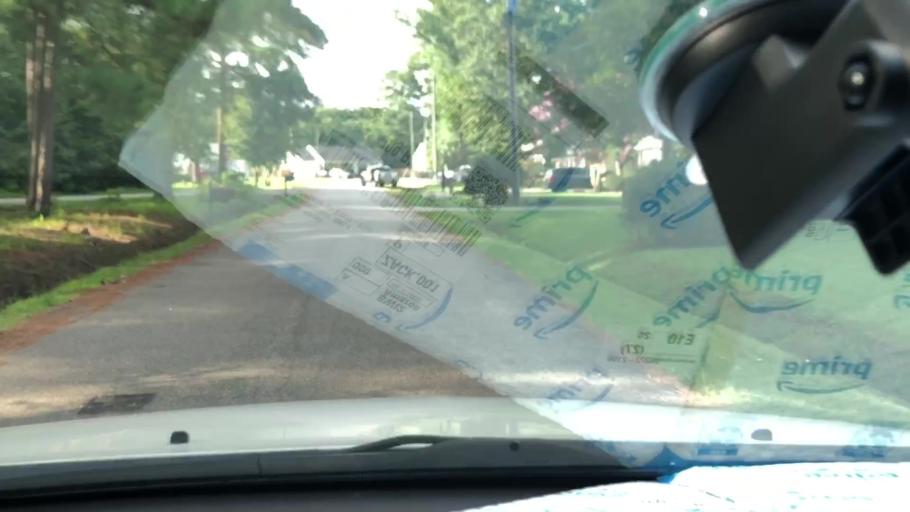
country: US
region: Virginia
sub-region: City of Chesapeake
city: Chesapeake
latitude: 36.7034
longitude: -76.2758
